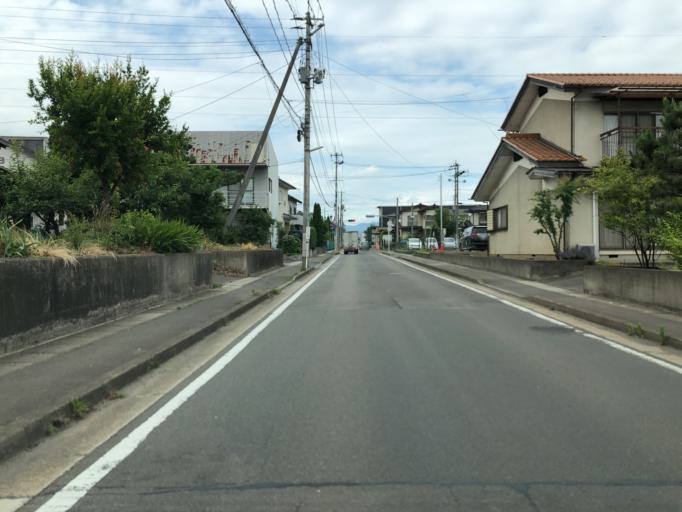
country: JP
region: Fukushima
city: Fukushima-shi
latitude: 37.7620
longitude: 140.4275
